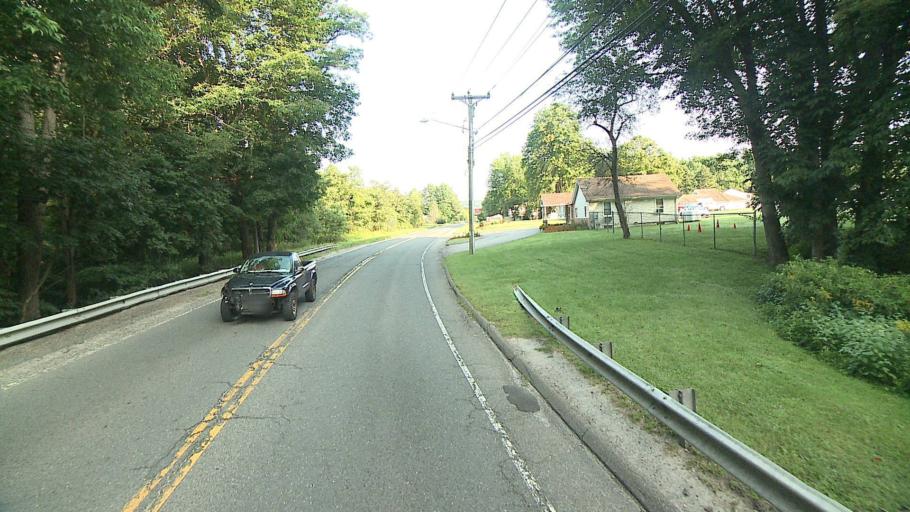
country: US
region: Connecticut
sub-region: Litchfield County
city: New Milford
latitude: 41.5834
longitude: -73.4422
